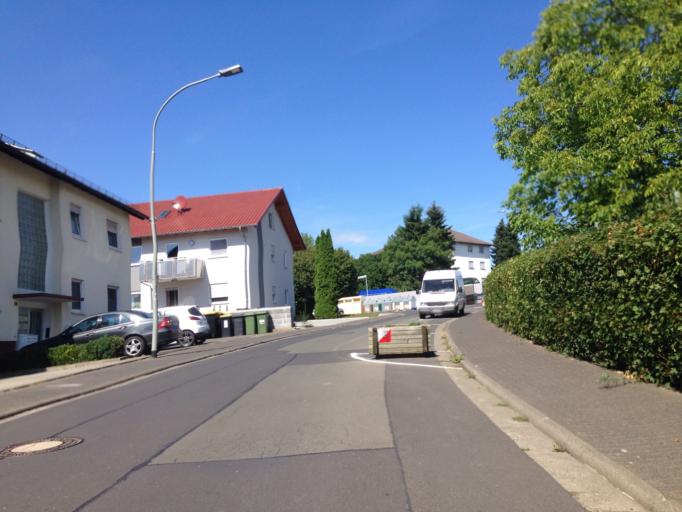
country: DE
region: Hesse
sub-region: Regierungsbezirk Giessen
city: Grunberg
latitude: 50.5932
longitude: 8.9482
